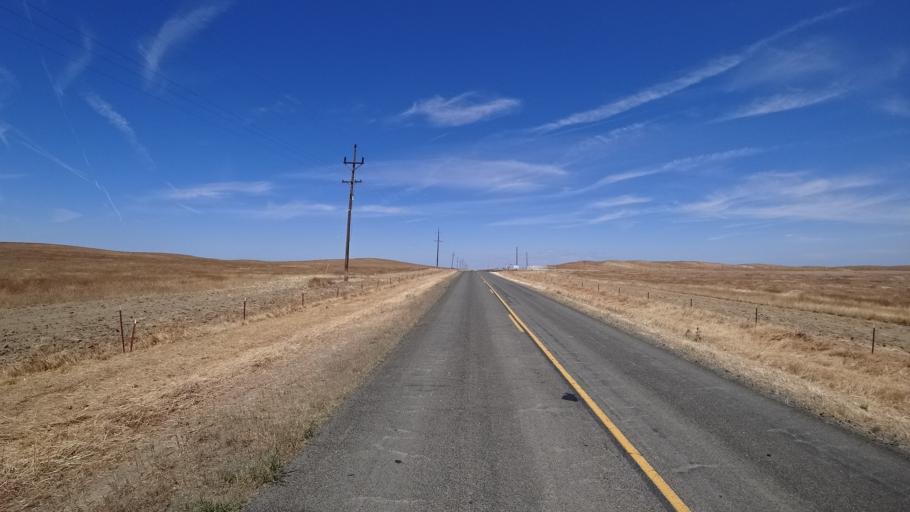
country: US
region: California
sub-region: Kings County
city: Kettleman City
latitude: 35.8571
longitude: -119.9153
